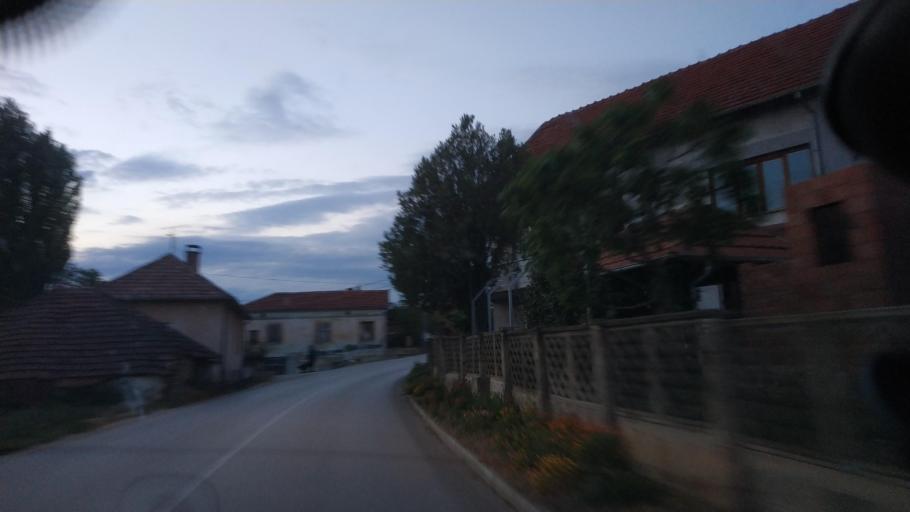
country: RS
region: Central Serbia
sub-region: Nisavski Okrug
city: Merosina
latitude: 43.2959
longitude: 21.7044
